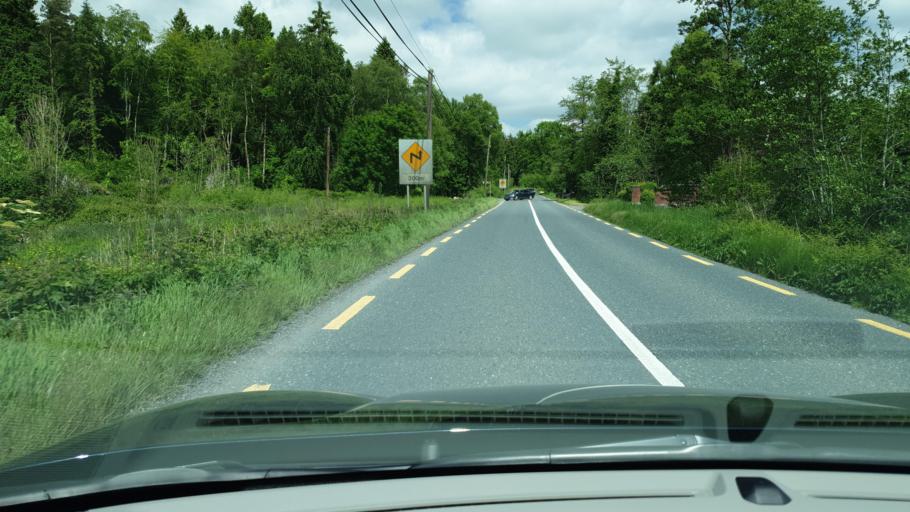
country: IE
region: Ulster
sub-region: An Cabhan
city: Kingscourt
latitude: 53.9110
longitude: -6.7880
